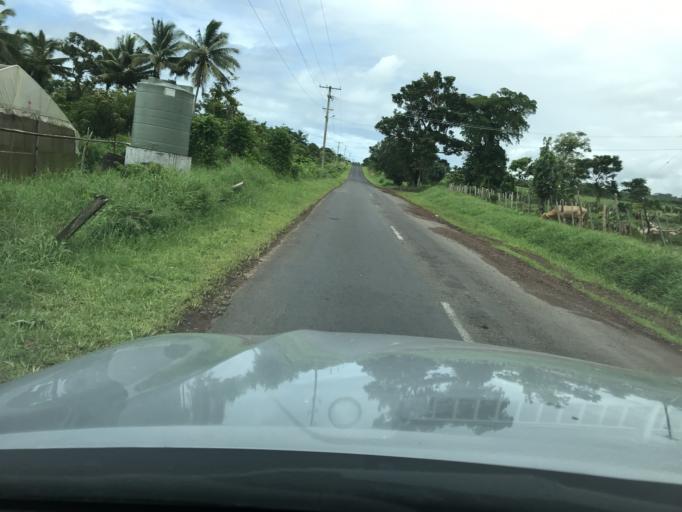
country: WS
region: A'ana
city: Leulumoega
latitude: -13.8763
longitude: -171.9342
